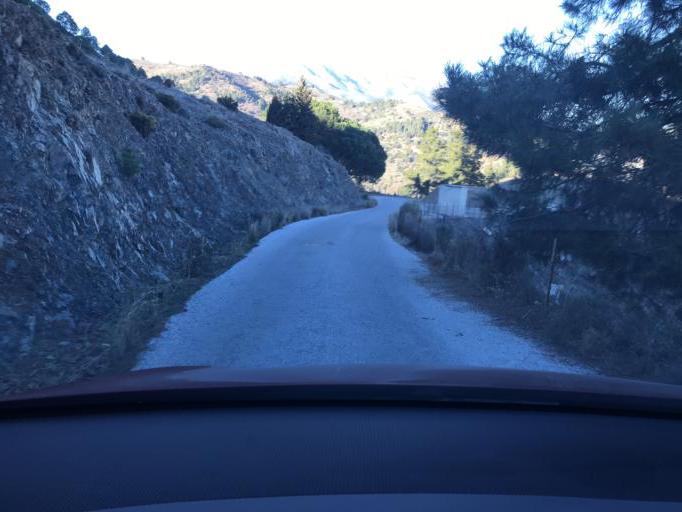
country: ES
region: Andalusia
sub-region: Provincia de Malaga
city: Tolox
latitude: 36.6825
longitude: -4.9144
